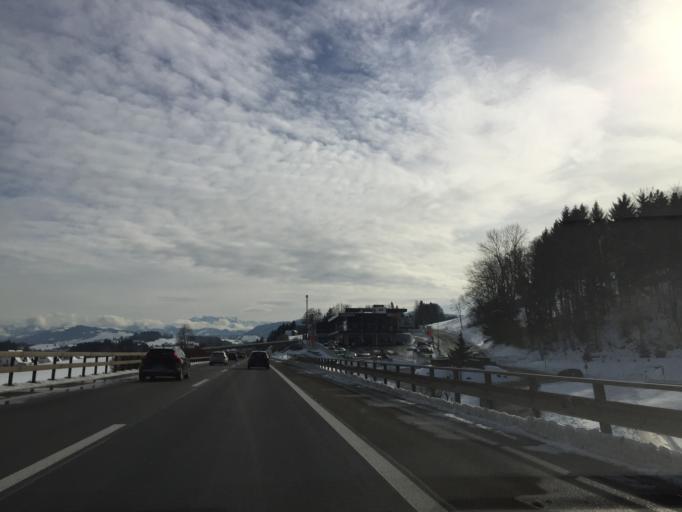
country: CH
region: Zurich
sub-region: Bezirk Horgen
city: Horgen / Allmend
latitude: 47.2393
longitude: 8.6105
